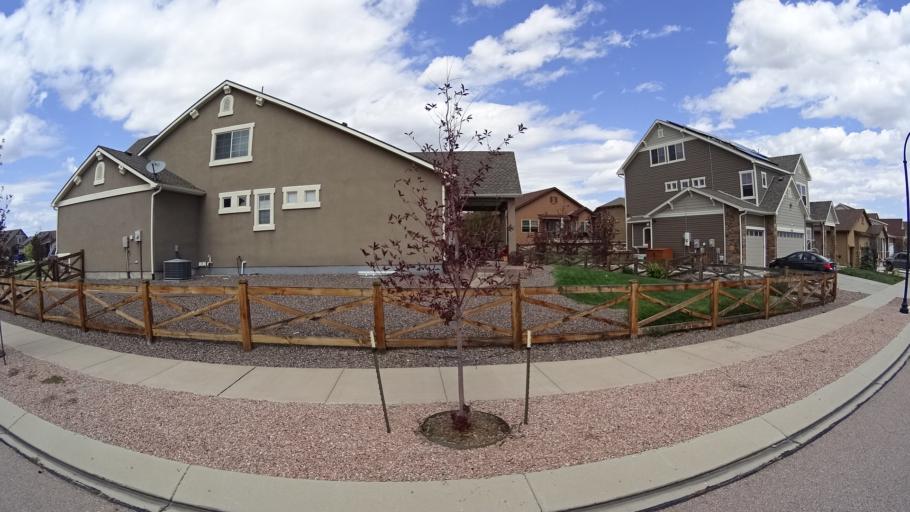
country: US
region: Colorado
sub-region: El Paso County
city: Black Forest
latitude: 38.9363
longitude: -104.6756
